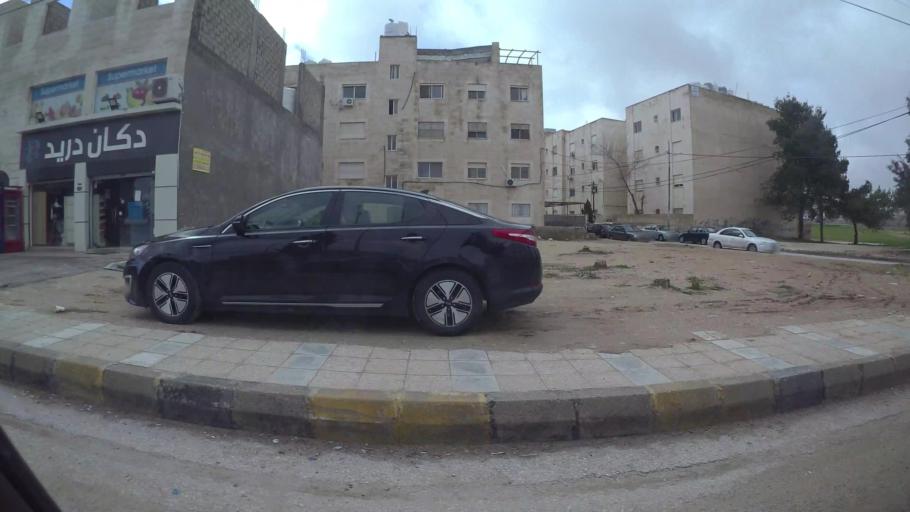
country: JO
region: Amman
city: Al Jubayhah
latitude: 32.0563
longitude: 35.8719
